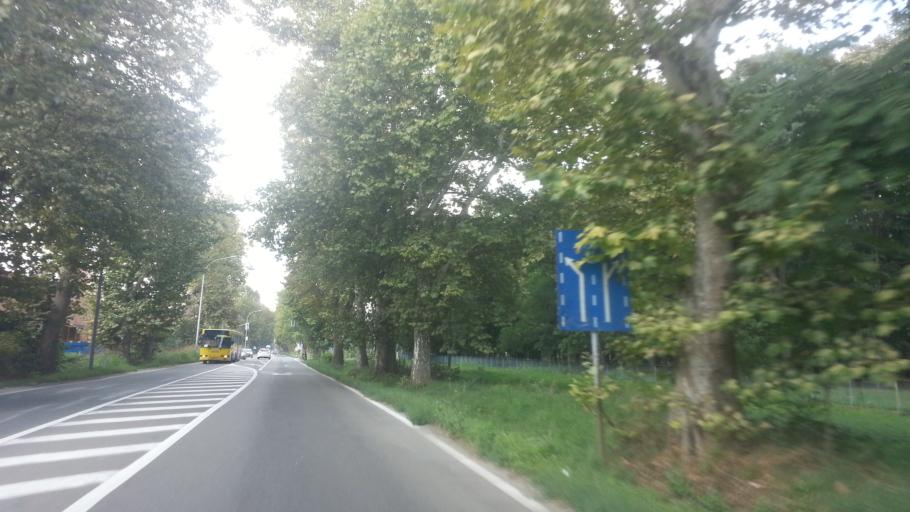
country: RS
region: Central Serbia
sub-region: Belgrade
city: Zemun
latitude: 44.8624
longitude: 20.3704
